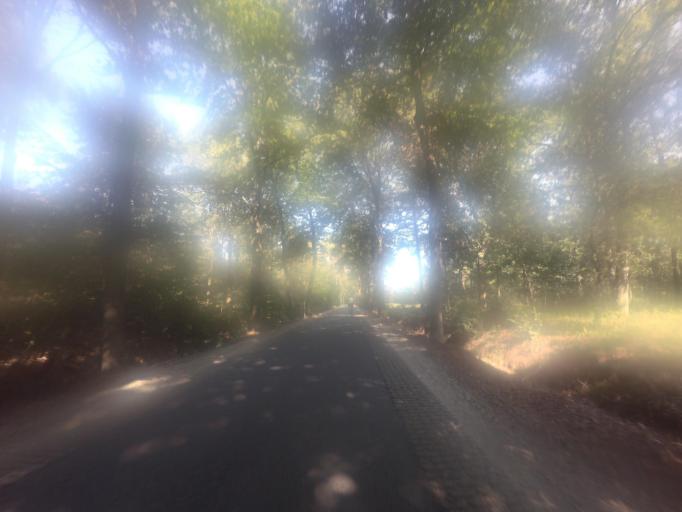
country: NL
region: North Brabant
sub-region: Gemeente Oirschot
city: Oostelbeers
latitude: 51.4903
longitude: 5.2661
